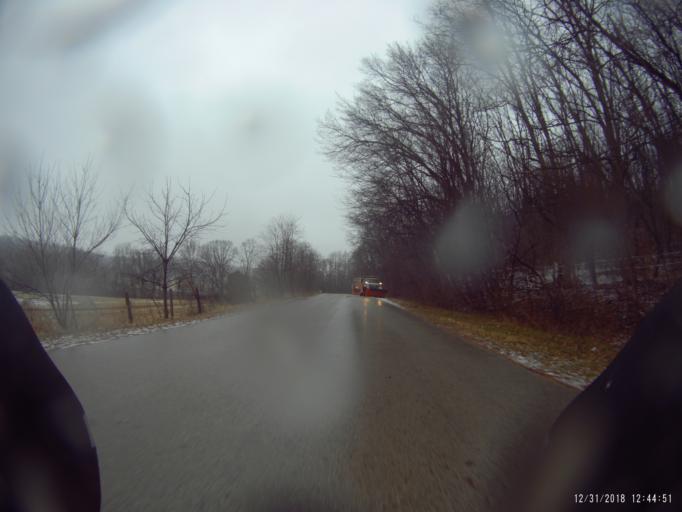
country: US
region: Wisconsin
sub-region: Dane County
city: Verona
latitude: 43.0344
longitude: -89.5084
